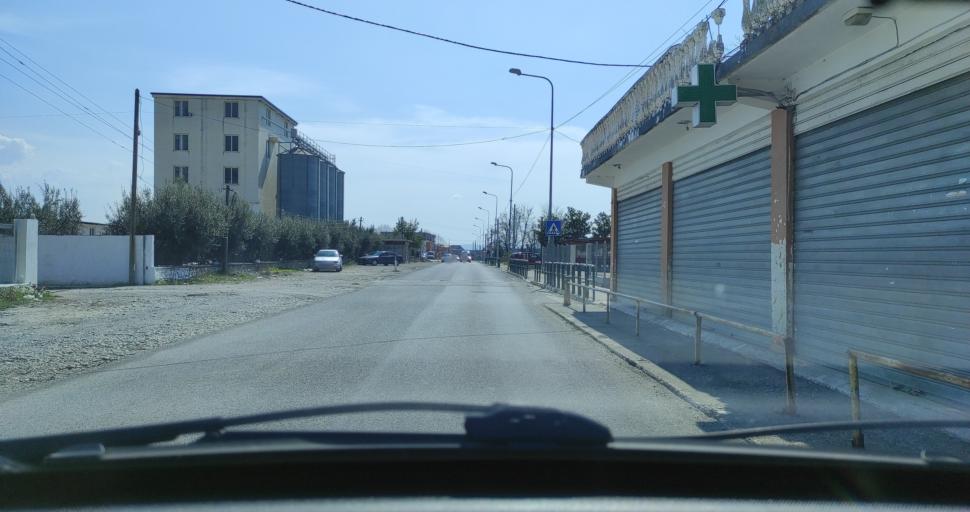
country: AL
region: Shkoder
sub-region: Rrethi i Shkodres
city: Vau i Dejes
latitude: 42.0040
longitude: 19.6178
